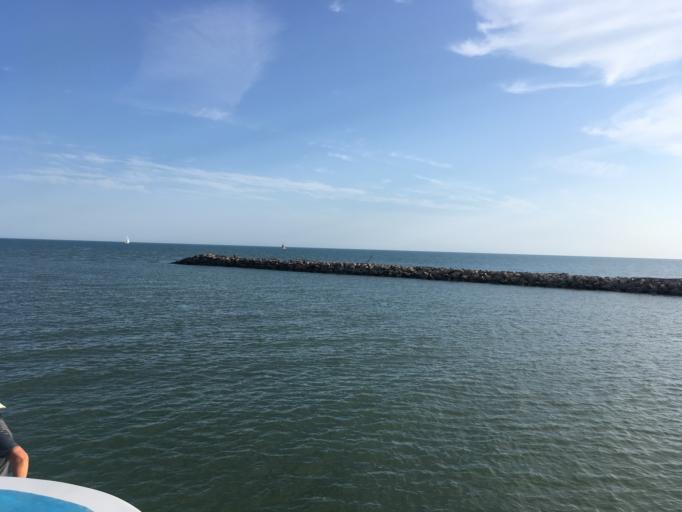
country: FR
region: Provence-Alpes-Cote d'Azur
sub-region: Departement des Bouches-du-Rhone
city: Saintes-Maries-de-la-Mer
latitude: 43.4509
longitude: 4.3970
